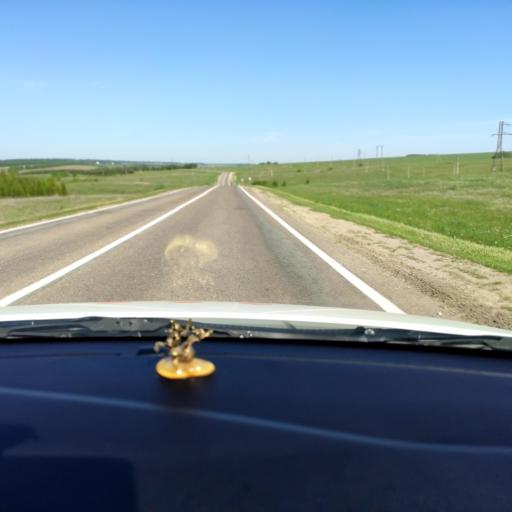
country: RU
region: Tatarstan
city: Vysokaya Gora
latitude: 56.0123
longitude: 49.2865
